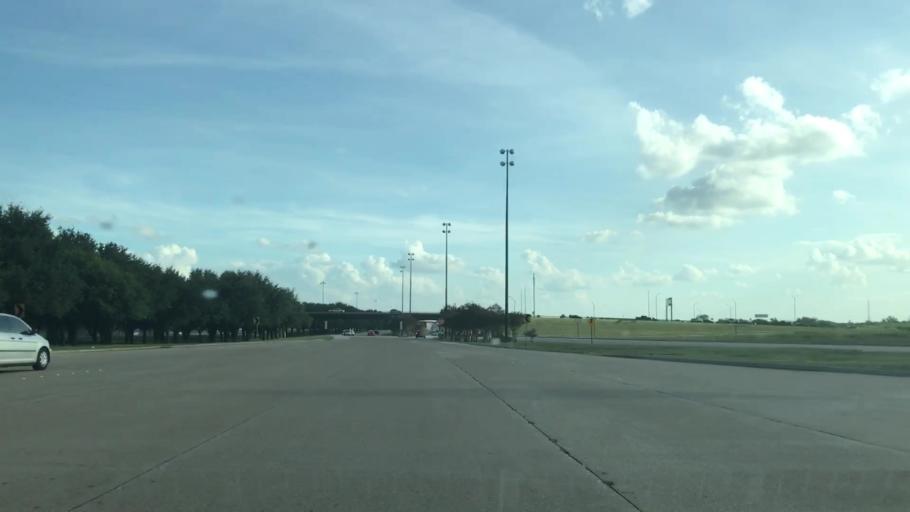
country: US
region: Texas
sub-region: Tarrant County
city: Euless
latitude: 32.8649
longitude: -97.0412
